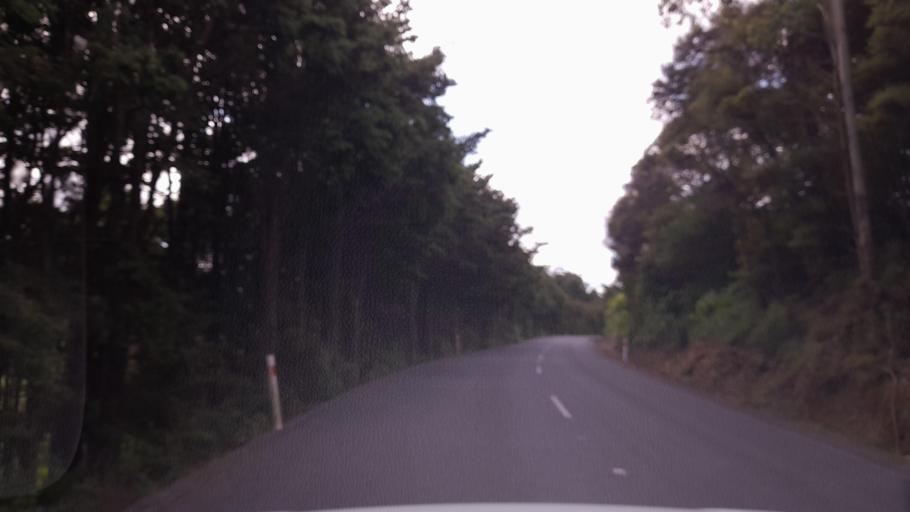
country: NZ
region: Northland
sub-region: Whangarei
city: Maungatapere
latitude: -35.6809
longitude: 174.0400
